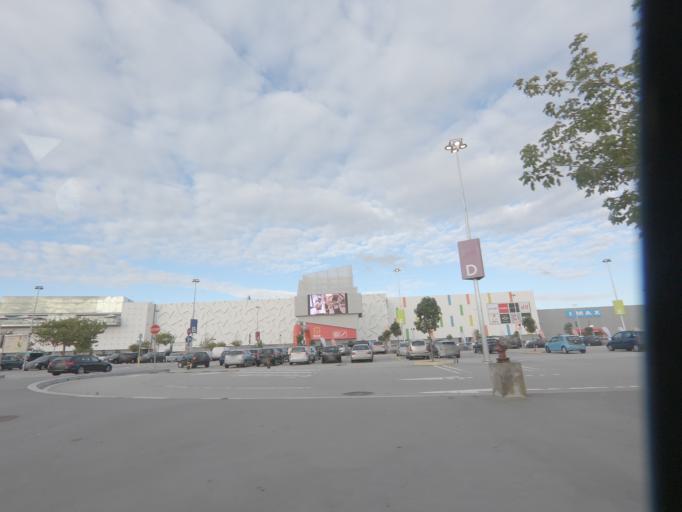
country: PT
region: Porto
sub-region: Matosinhos
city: Santa Cruz do Bispo
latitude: 41.2083
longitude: -8.6895
